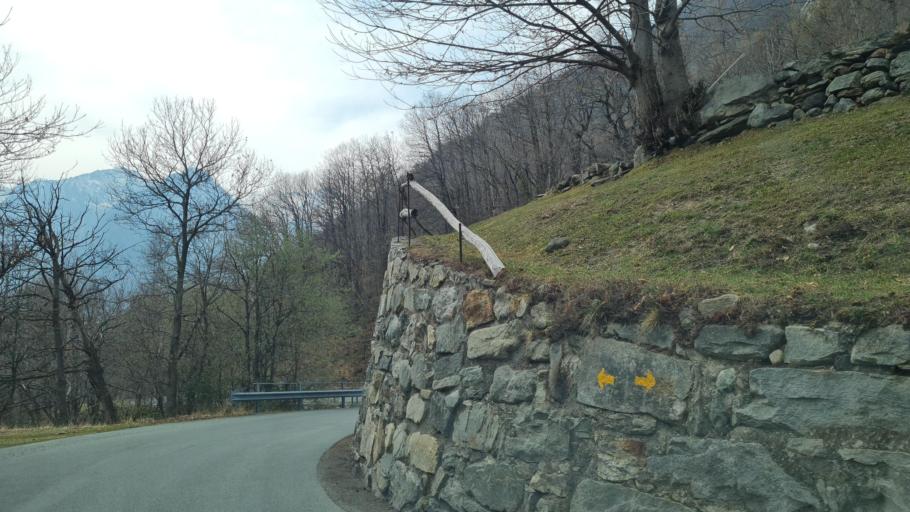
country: IT
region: Aosta Valley
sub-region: Valle d'Aosta
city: Pont-Bozet
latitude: 45.6140
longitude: 7.7052
